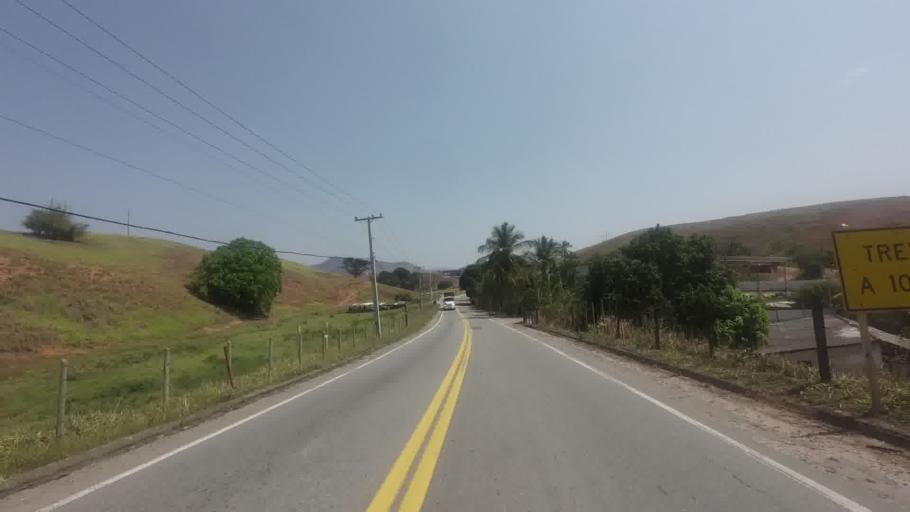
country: BR
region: Espirito Santo
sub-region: Cachoeiro De Itapemirim
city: Cachoeiro de Itapemirim
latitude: -20.8579
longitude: -41.0779
